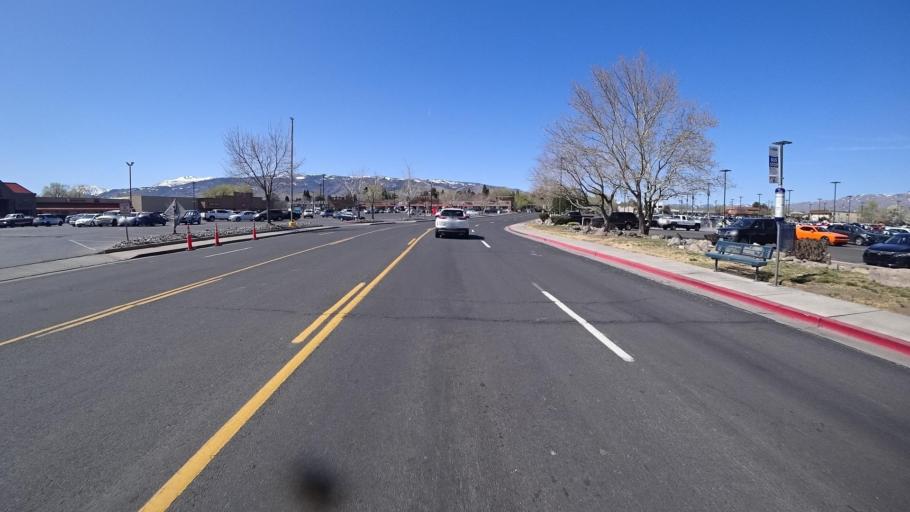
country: US
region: Nevada
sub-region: Washoe County
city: Reno
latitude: 39.4877
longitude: -119.7956
